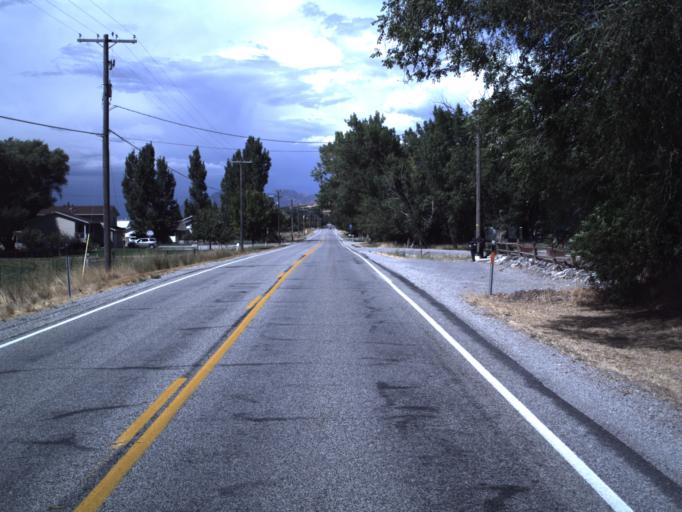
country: US
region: Utah
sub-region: Box Elder County
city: Elwood
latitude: 41.6934
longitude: -112.0900
